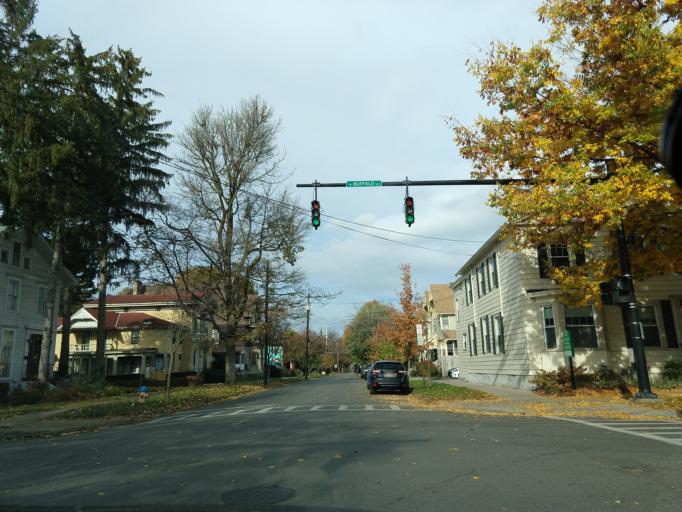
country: US
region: New York
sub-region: Tompkins County
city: Ithaca
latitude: 42.4412
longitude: -76.5009
